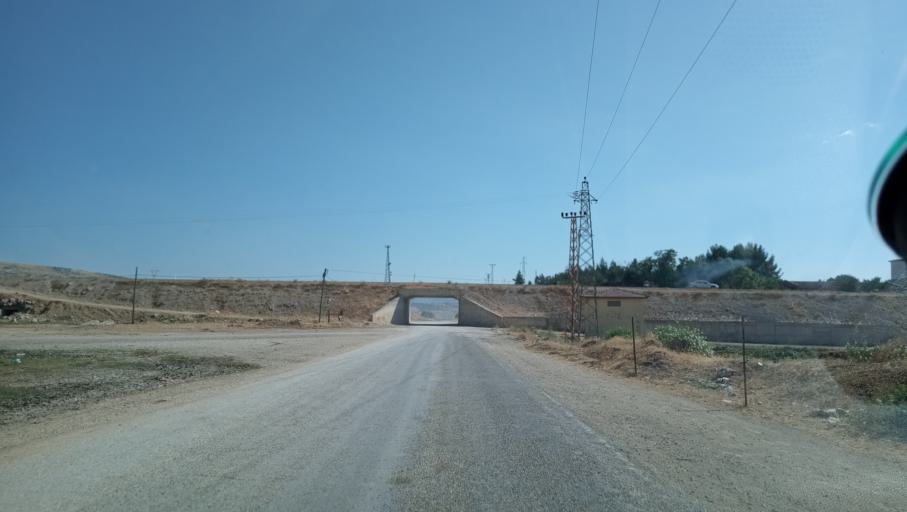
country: TR
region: Diyarbakir
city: Malabadi
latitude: 38.1373
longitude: 41.1914
